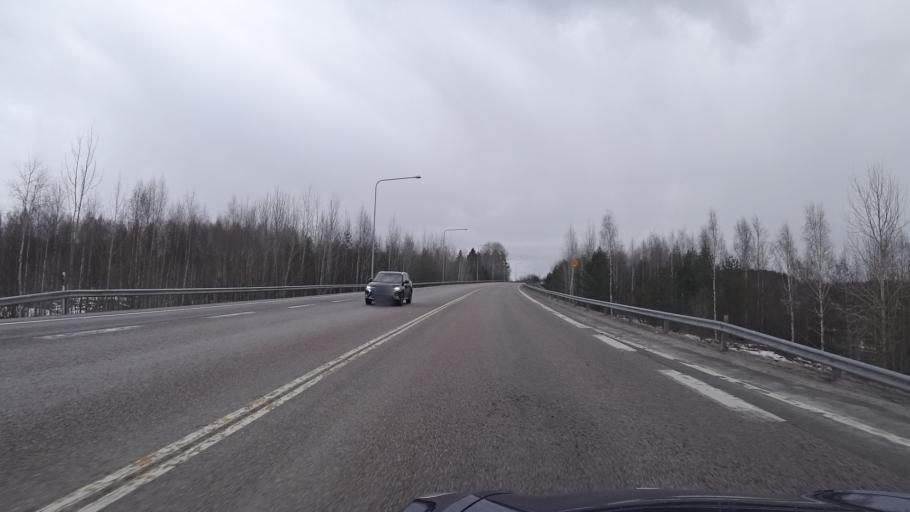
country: FI
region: Paijanne Tavastia
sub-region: Lahti
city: Nastola
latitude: 60.9444
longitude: 25.8916
